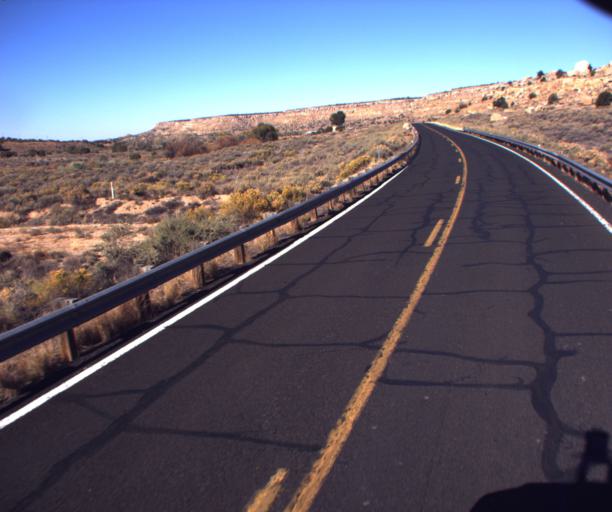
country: US
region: Arizona
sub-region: Navajo County
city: First Mesa
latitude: 35.8389
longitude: -110.2326
